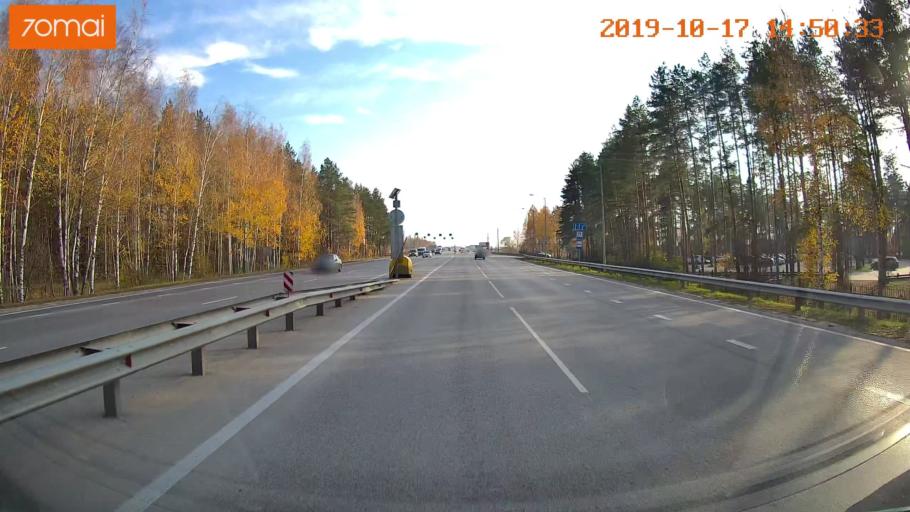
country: RU
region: Rjazan
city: Polyany
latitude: 54.7323
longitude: 39.8430
